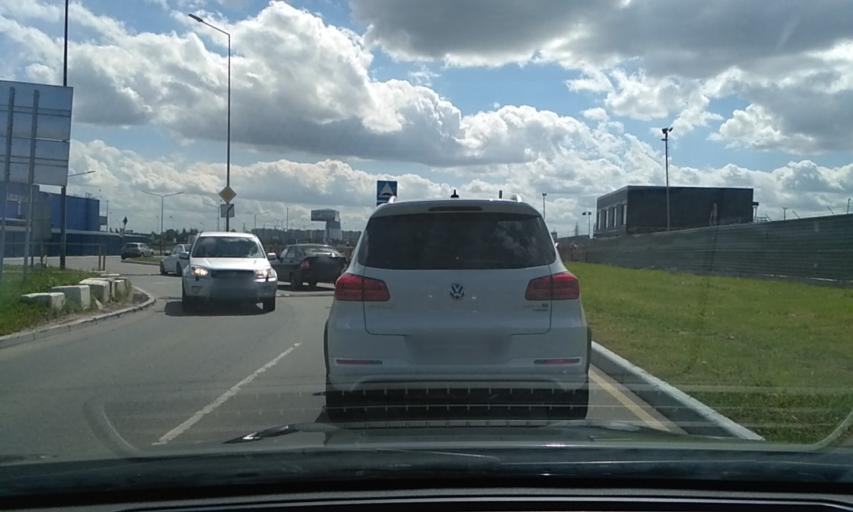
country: RU
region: Leningrad
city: Rybatskoye
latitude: 59.8934
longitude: 30.5087
